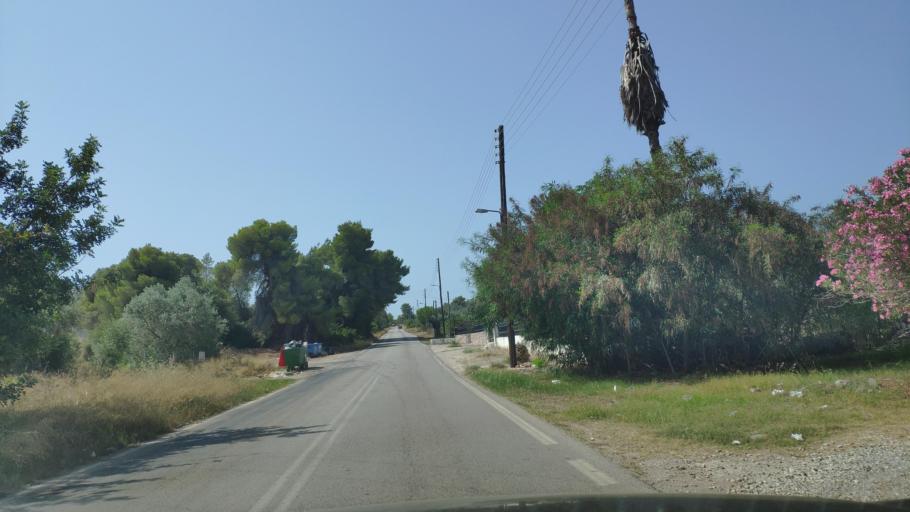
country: GR
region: Peloponnese
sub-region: Nomos Argolidos
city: Porto Cheli
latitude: 37.3064
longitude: 23.1643
